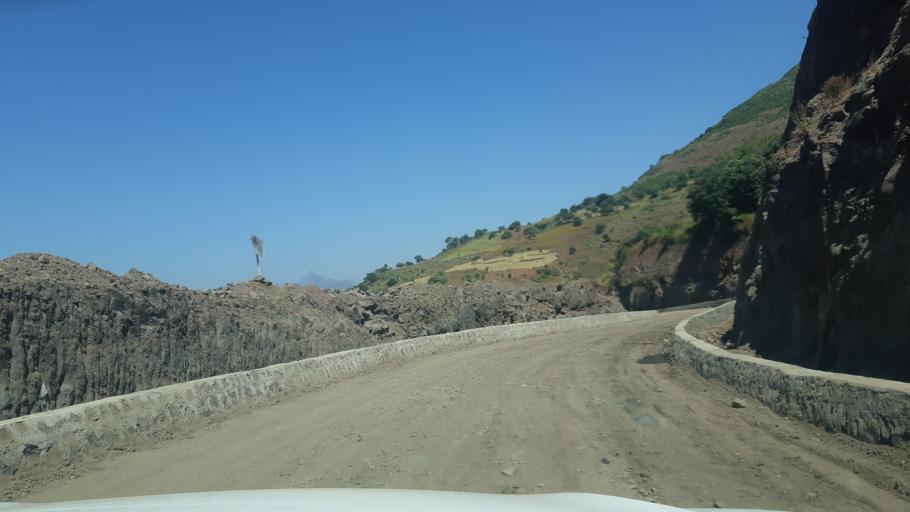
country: ET
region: Amhara
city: Dabat
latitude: 13.1663
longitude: 37.6056
